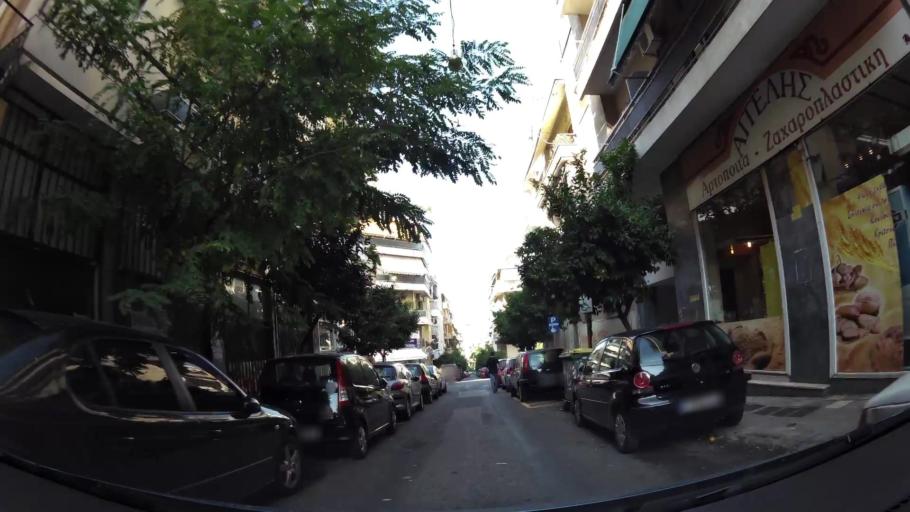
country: GR
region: Attica
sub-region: Nomarchia Athinas
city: Kaisariani
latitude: 37.9794
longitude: 23.7684
